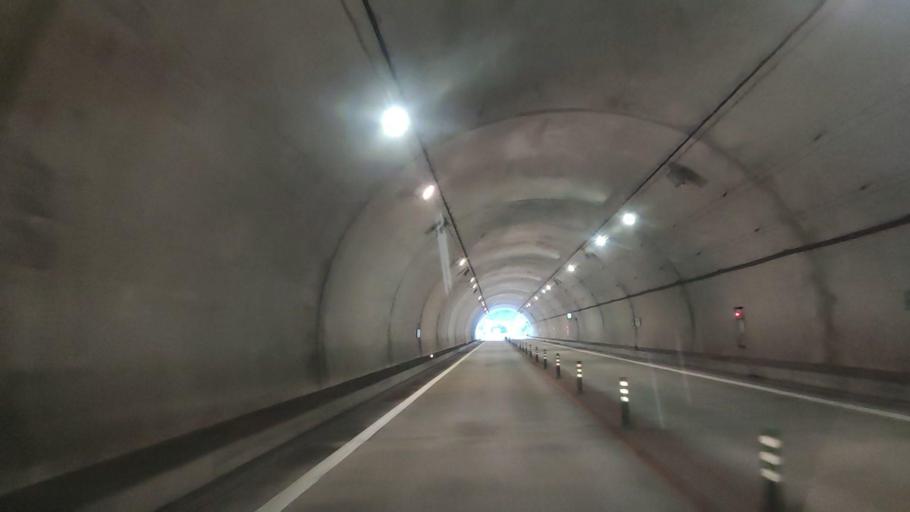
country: JP
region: Toyama
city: Himi
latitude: 36.9351
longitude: 137.0164
